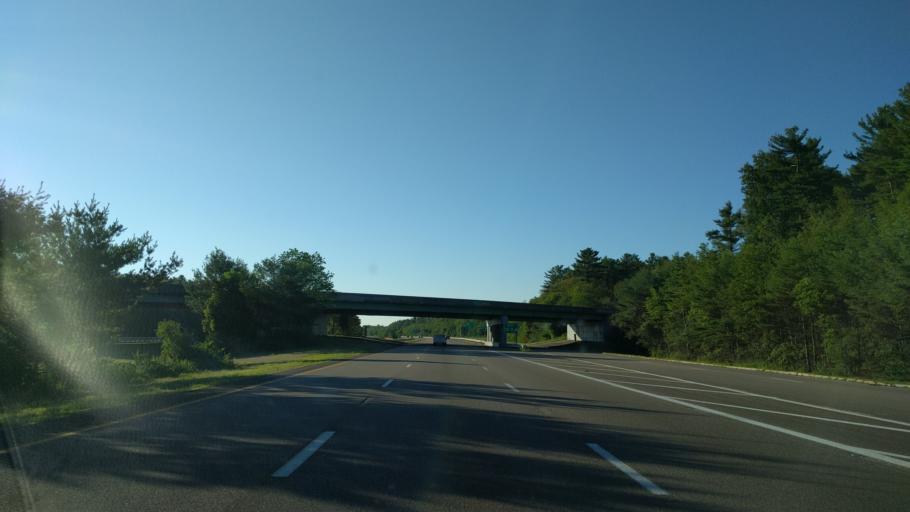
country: US
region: Massachusetts
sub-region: Bristol County
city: Mansfield Center
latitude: 42.0072
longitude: -71.2258
